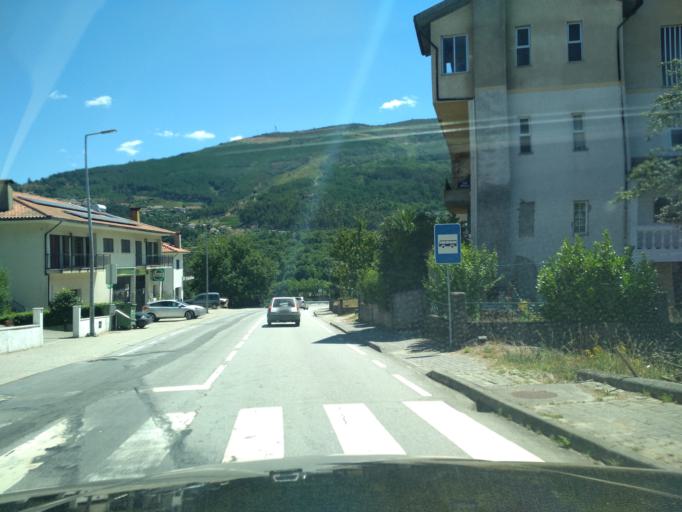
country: PT
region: Vila Real
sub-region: Ribeira de Pena
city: Sobreira
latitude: 41.5272
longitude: -7.7917
